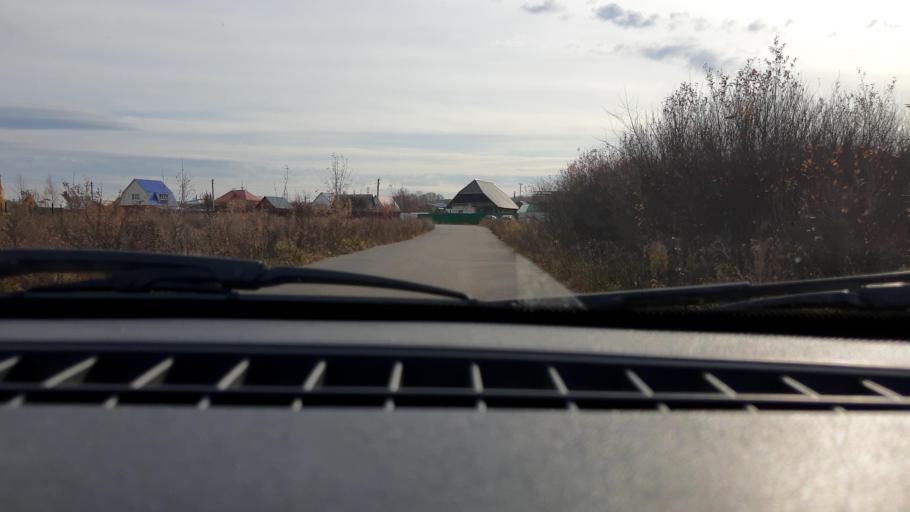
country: RU
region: Bashkortostan
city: Ufa
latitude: 54.5960
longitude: 55.8989
